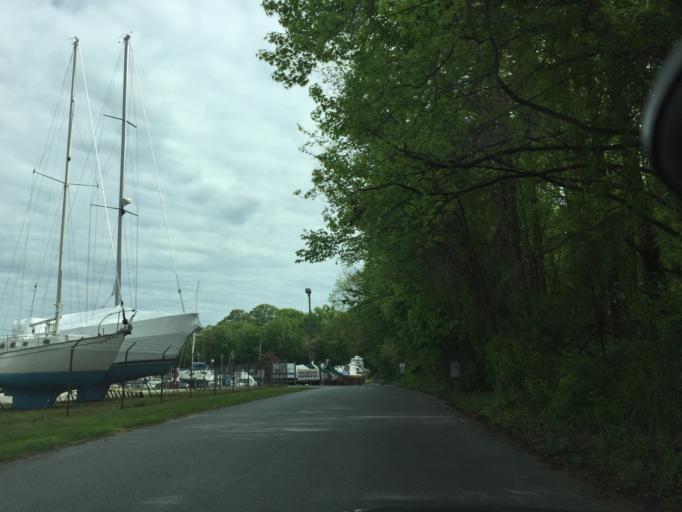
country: US
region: Maryland
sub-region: Baltimore County
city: Middle River
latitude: 39.3225
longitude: -76.4422
